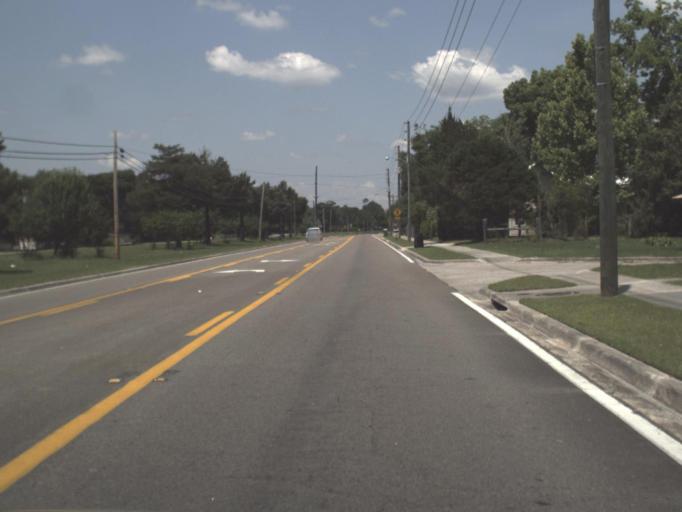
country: US
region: Florida
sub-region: Union County
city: Lake Butler
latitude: 30.0241
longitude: -82.3467
